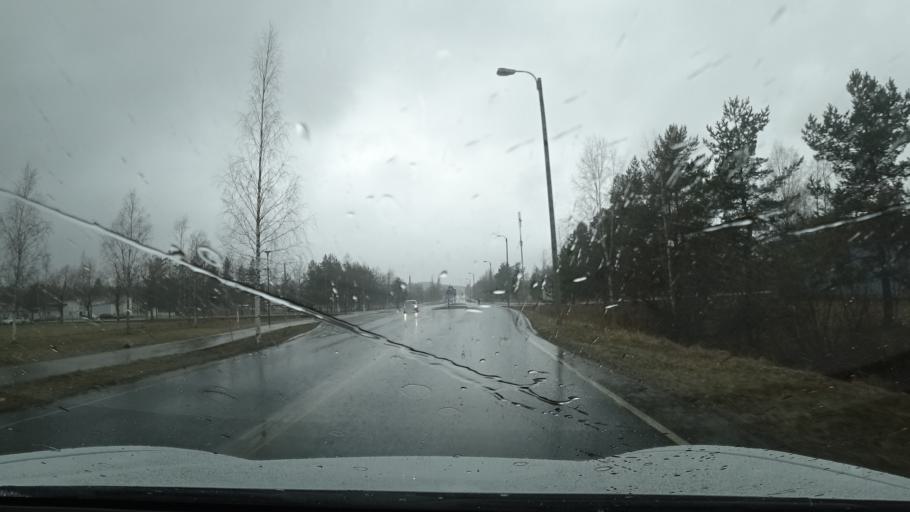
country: FI
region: Paijanne Tavastia
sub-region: Lahti
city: Orimattila
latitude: 60.8024
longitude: 25.7498
